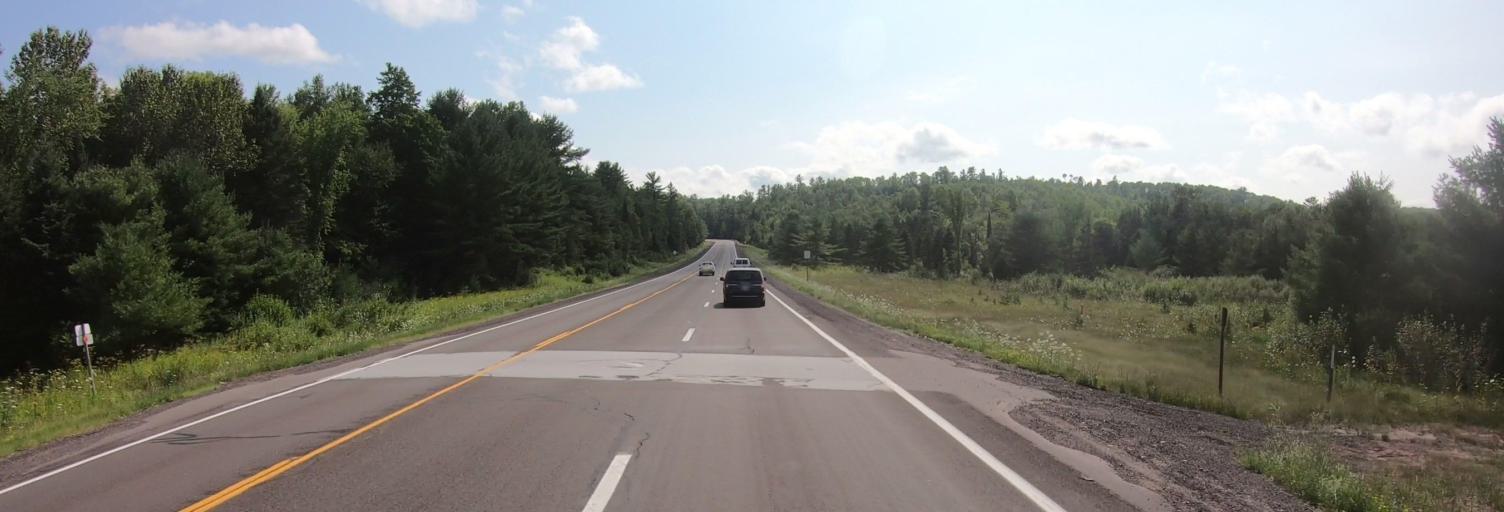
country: US
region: Michigan
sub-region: Ontonagon County
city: Ontonagon
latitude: 46.6973
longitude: -89.1621
